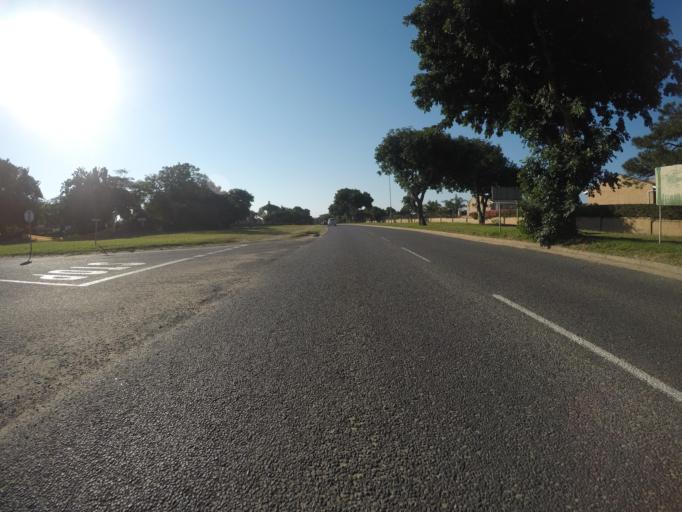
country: ZA
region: KwaZulu-Natal
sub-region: uThungulu District Municipality
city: Richards Bay
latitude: -28.7887
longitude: 32.0990
